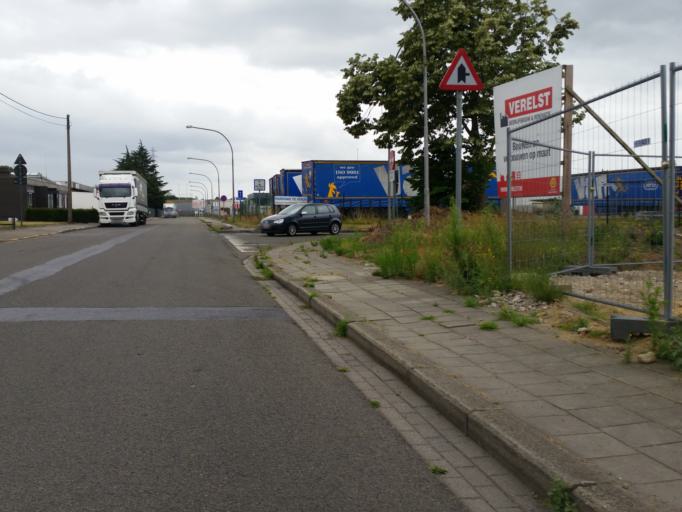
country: BE
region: Flanders
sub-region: Provincie Antwerpen
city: Mechelen
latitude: 51.0528
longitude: 4.4597
